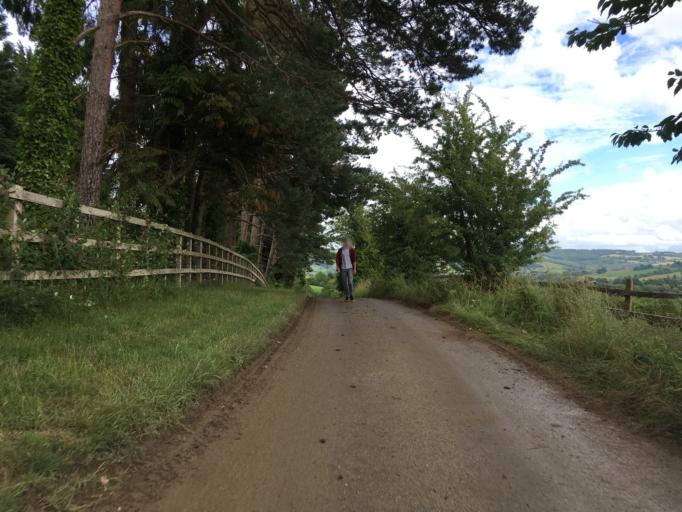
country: GB
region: England
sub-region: Gloucestershire
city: Winchcombe
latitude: 51.9513
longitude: -1.9974
